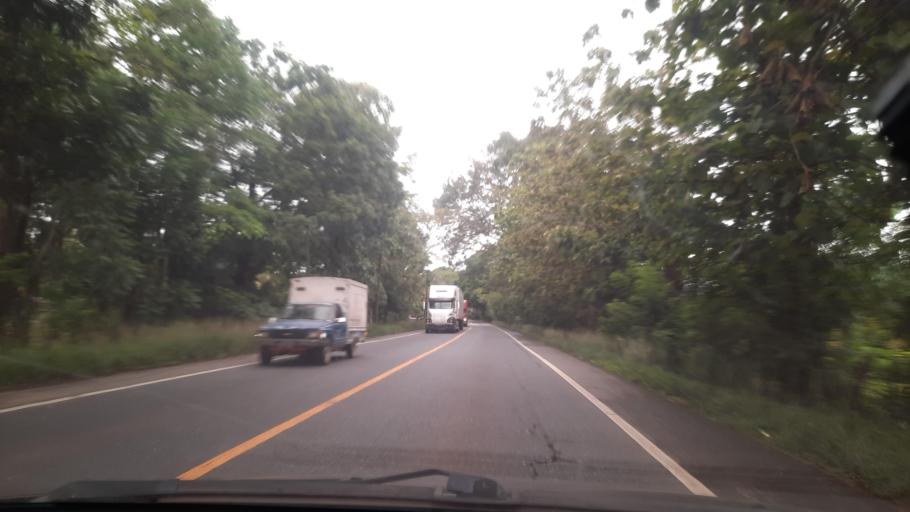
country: GT
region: Izabal
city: Morales
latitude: 15.4454
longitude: -88.9459
